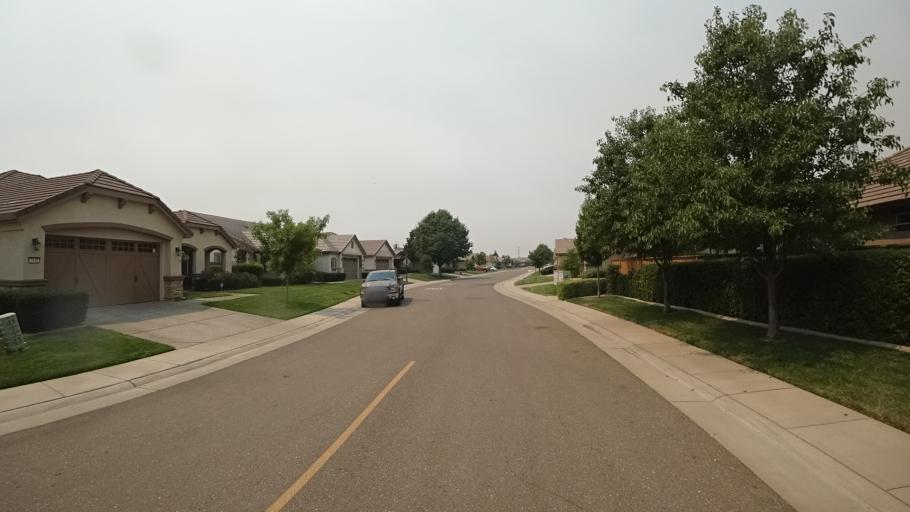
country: US
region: California
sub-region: Sacramento County
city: Laguna
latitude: 38.3953
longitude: -121.4141
